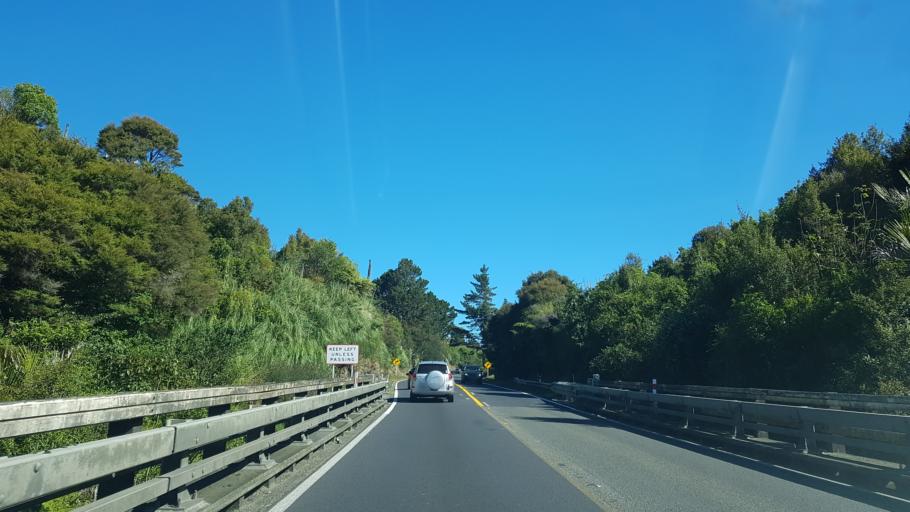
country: NZ
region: Auckland
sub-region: Auckland
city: Warkworth
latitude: -36.4594
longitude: 174.6526
